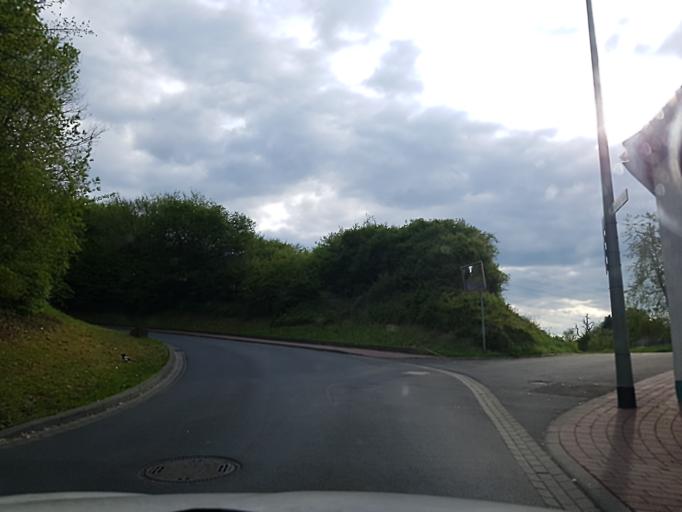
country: DE
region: Hesse
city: Bad Camberg
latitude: 50.2792
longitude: 8.2058
